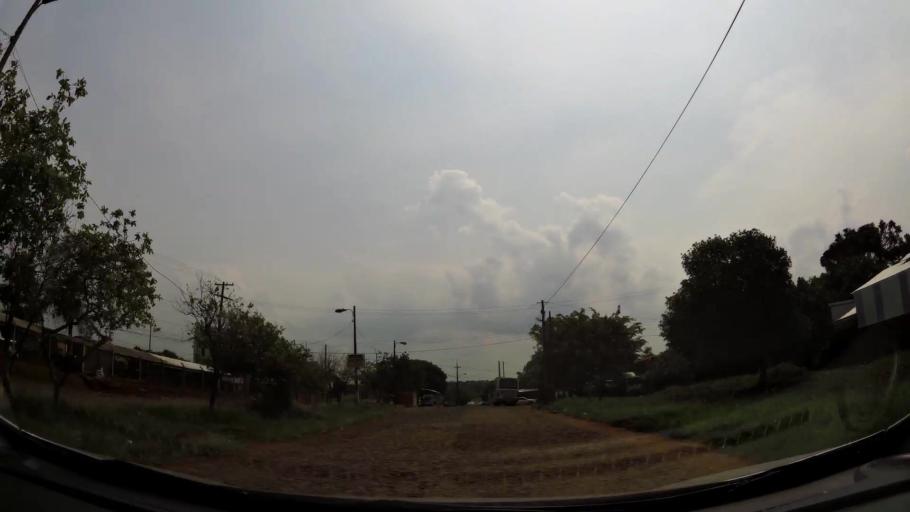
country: PY
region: Alto Parana
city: Presidente Franco
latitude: -25.5457
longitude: -54.6302
